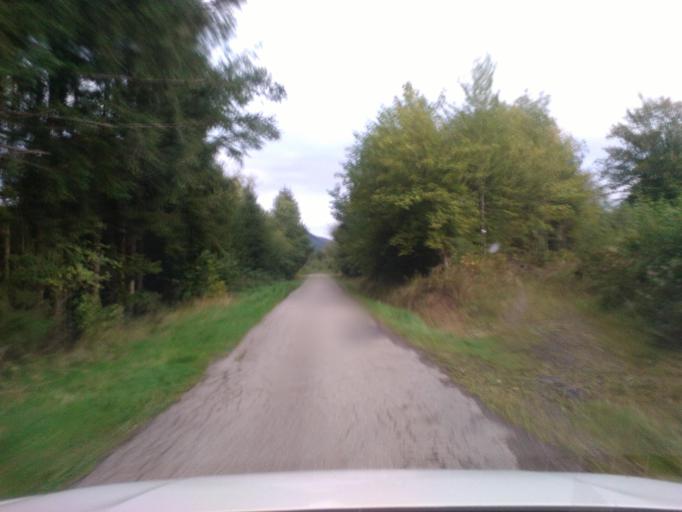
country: FR
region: Lorraine
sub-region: Departement des Vosges
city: Senones
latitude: 48.3948
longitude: 7.0375
